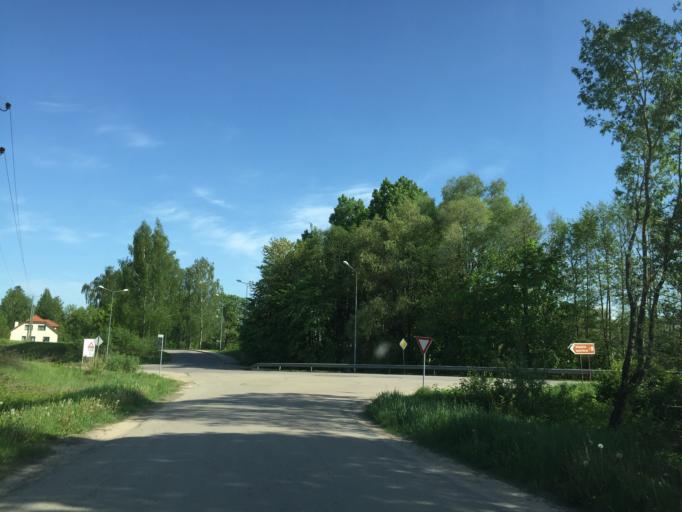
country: LV
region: Salaspils
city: Salaspils
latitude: 56.8216
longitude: 24.4245
